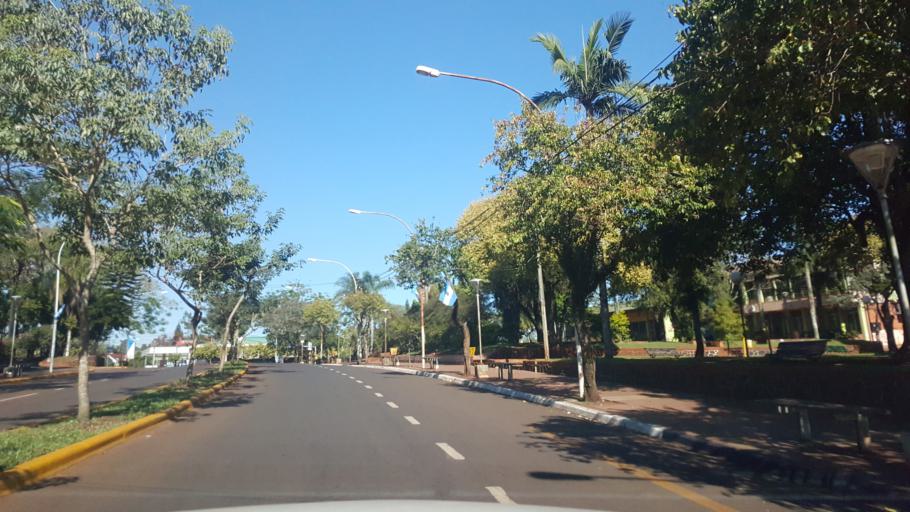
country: AR
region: Misiones
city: Puerto Rico
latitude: -26.8167
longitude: -55.0273
